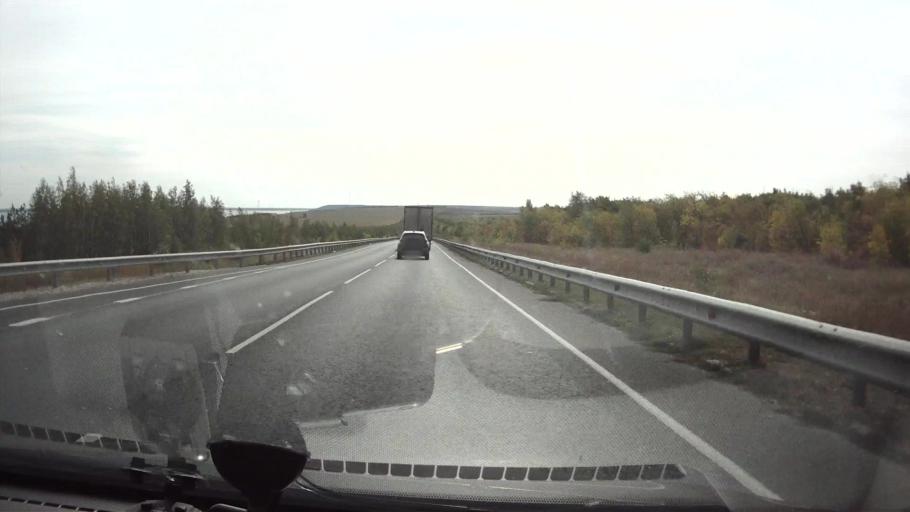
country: RU
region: Saratov
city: Balakovo
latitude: 52.1584
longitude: 47.8192
